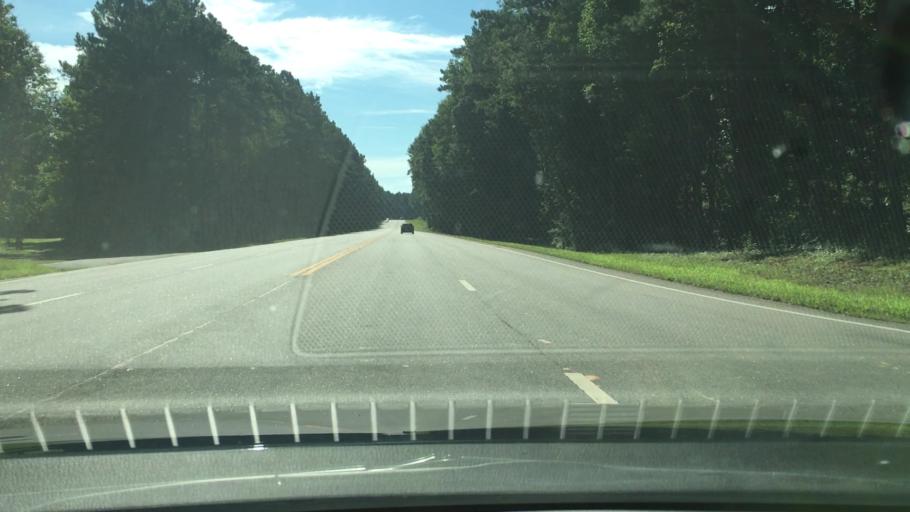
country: US
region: Georgia
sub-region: Putnam County
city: Jefferson
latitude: 33.4375
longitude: -83.3870
